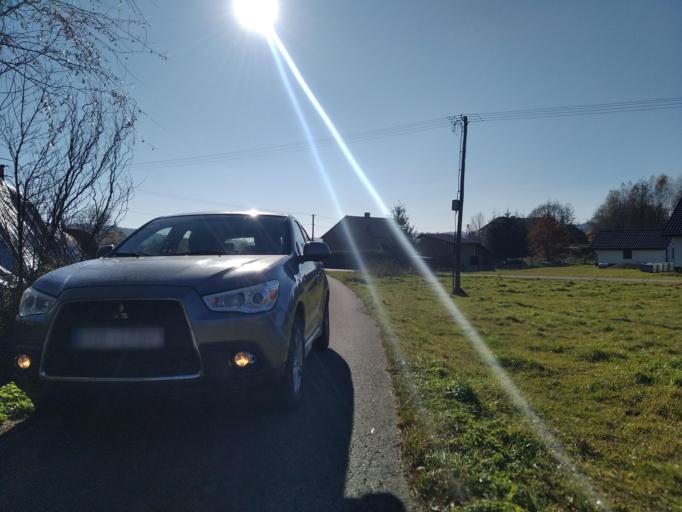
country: PL
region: Subcarpathian Voivodeship
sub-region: Powiat strzyzowski
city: Frysztak
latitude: 49.8508
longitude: 21.6122
